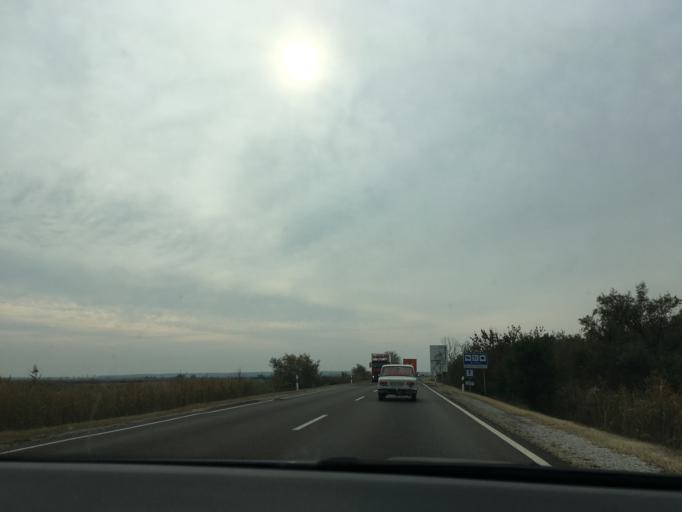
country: HU
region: Jasz-Nagykun-Szolnok
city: Kisujszallas
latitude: 47.2341
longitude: 20.8209
